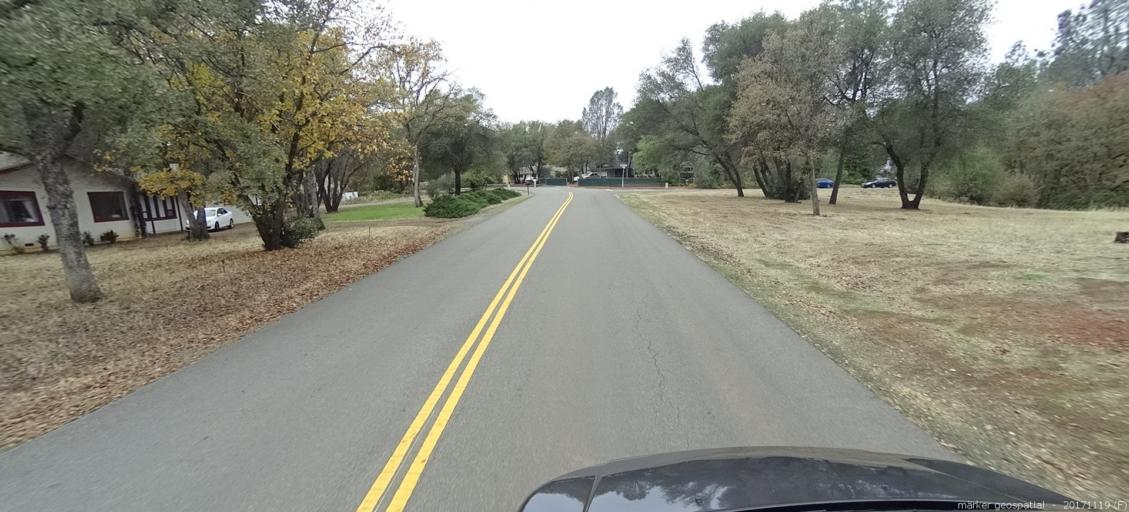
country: US
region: California
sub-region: Shasta County
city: Redding
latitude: 40.4900
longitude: -122.4198
